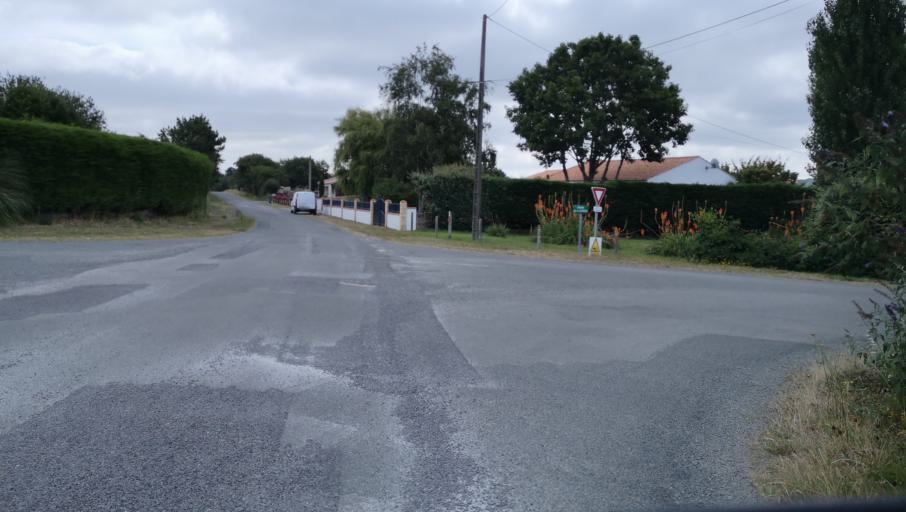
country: FR
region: Pays de la Loire
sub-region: Departement de la Vendee
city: Bretignolles-sur-Mer
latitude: 46.5961
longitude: -1.8174
